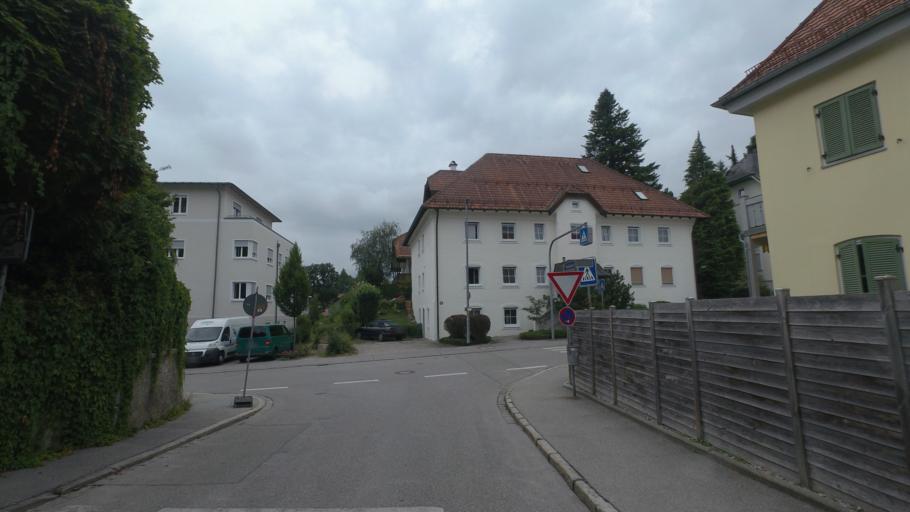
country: DE
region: Bavaria
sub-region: Upper Bavaria
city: Traunstein
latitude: 47.8649
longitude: 12.6365
